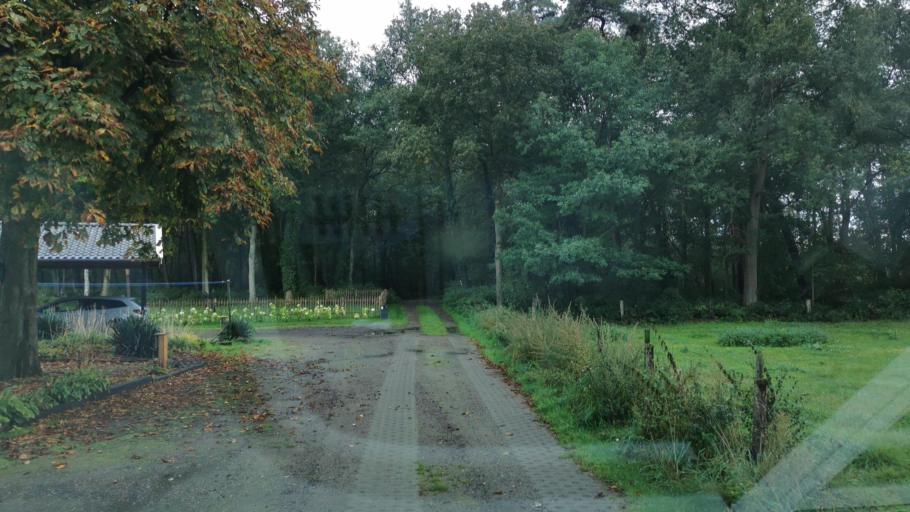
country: NL
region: Overijssel
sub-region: Gemeente Losser
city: Losser
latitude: 52.3041
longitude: 7.0289
